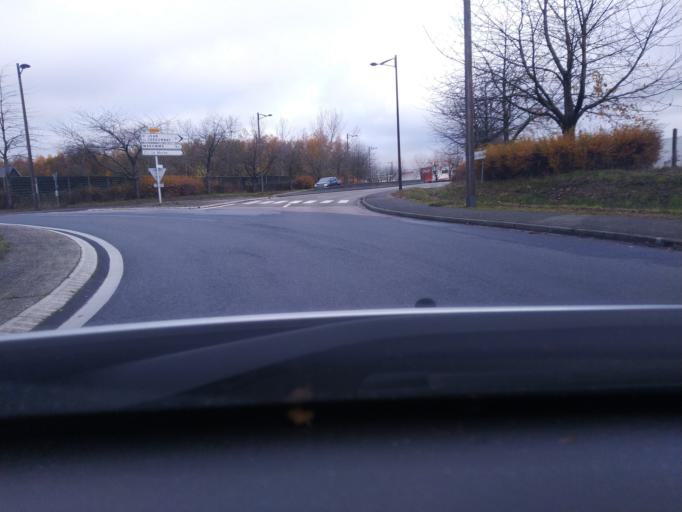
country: FR
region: Haute-Normandie
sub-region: Departement de la Seine-Maritime
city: Maromme
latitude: 49.4839
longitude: 1.0150
